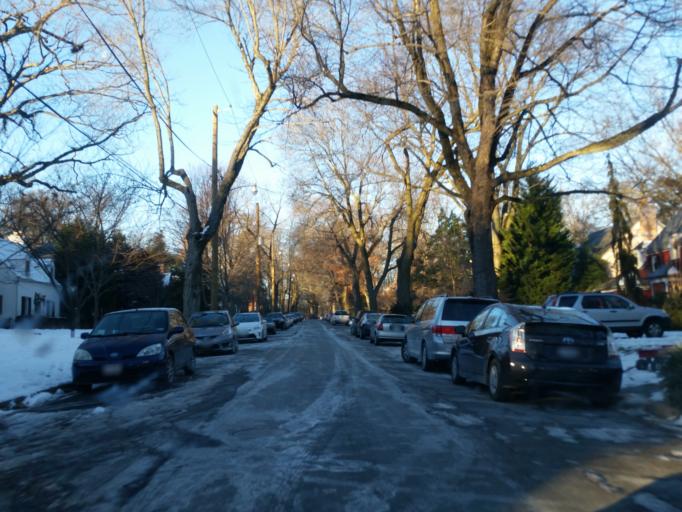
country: US
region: Maryland
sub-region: Montgomery County
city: Chevy Chase
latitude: 38.9759
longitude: -77.0629
